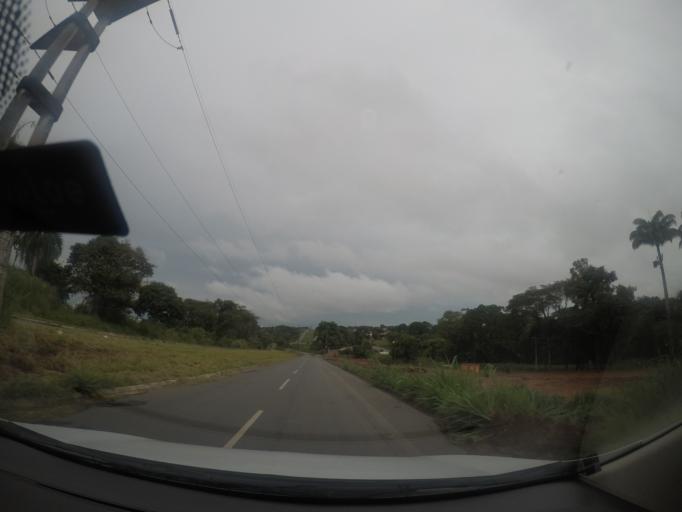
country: BR
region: Goias
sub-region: Aparecida De Goiania
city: Aparecida de Goiania
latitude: -16.7649
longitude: -49.3042
